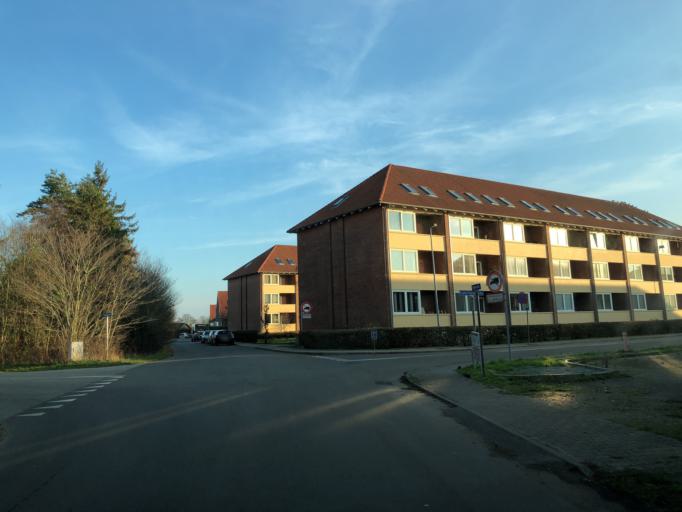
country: DK
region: South Denmark
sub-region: Fredericia Kommune
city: Fredericia
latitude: 55.5774
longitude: 9.7434
